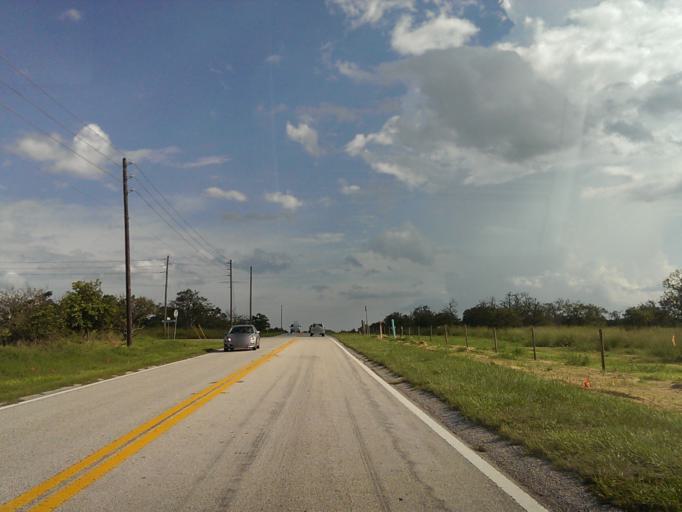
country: US
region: Florida
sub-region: Polk County
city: Citrus Ridge
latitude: 28.4134
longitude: -81.6359
